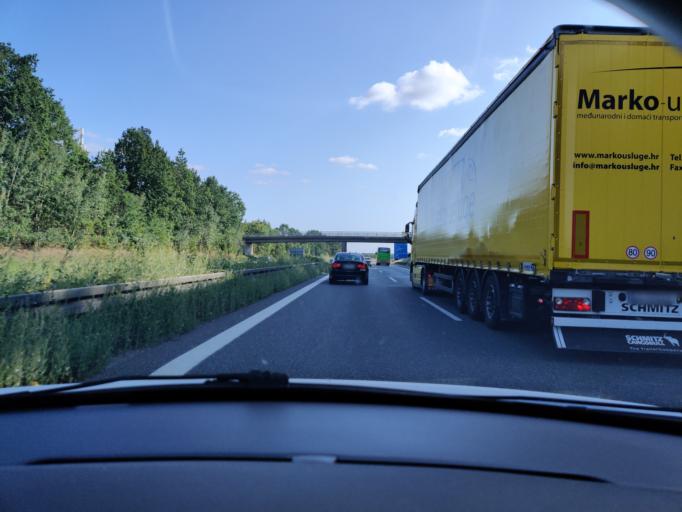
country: DE
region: Bavaria
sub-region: Upper Palatinate
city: Wackersdorf
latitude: 49.3240
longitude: 12.1543
